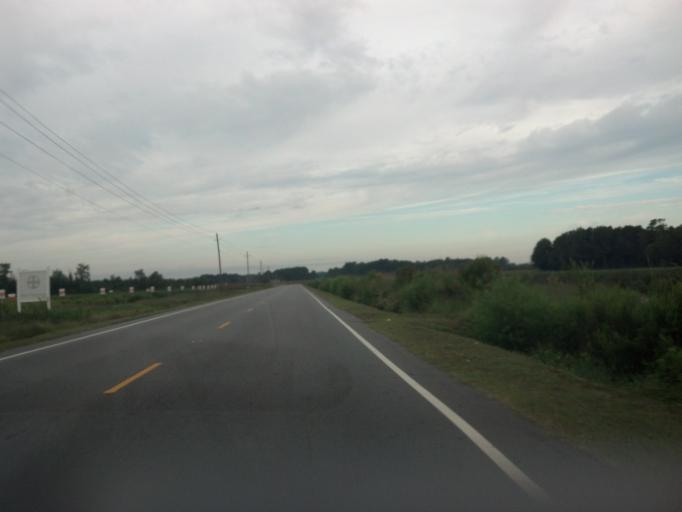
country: US
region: North Carolina
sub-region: Pitt County
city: Ayden
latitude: 35.4764
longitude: -77.4444
